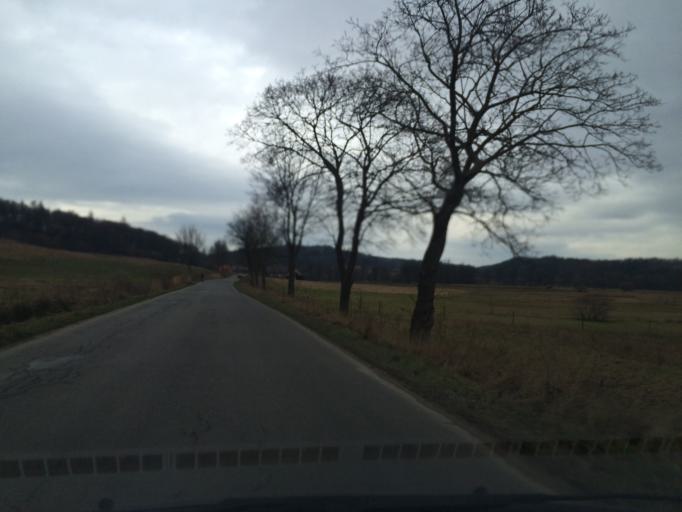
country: PL
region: Lower Silesian Voivodeship
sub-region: Powiat lwowecki
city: Lwowek Slaski
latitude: 51.1184
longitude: 15.5564
